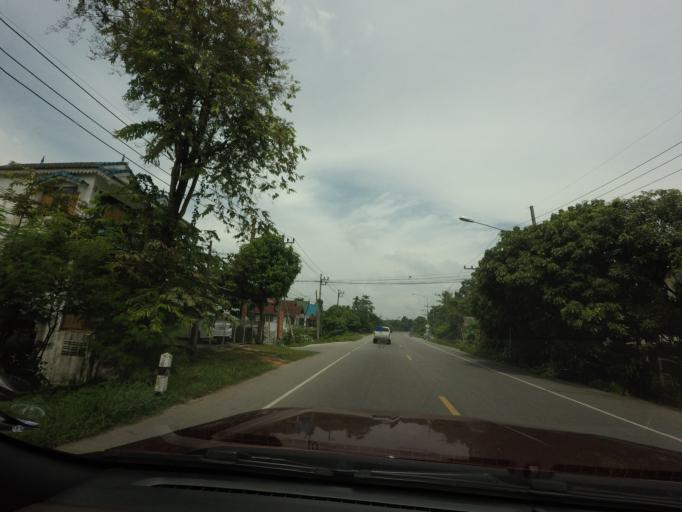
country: TH
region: Yala
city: Yala
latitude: 6.6093
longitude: 101.3058
